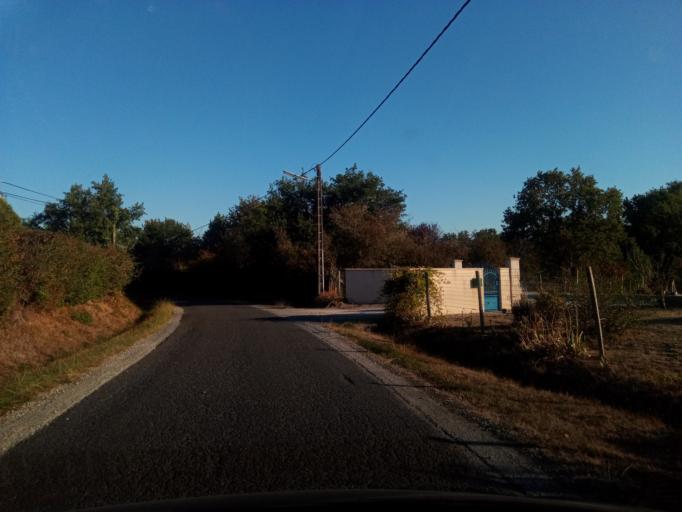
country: FR
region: Poitou-Charentes
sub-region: Departement de la Vienne
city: Montmorillon
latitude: 46.4170
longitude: 0.8654
